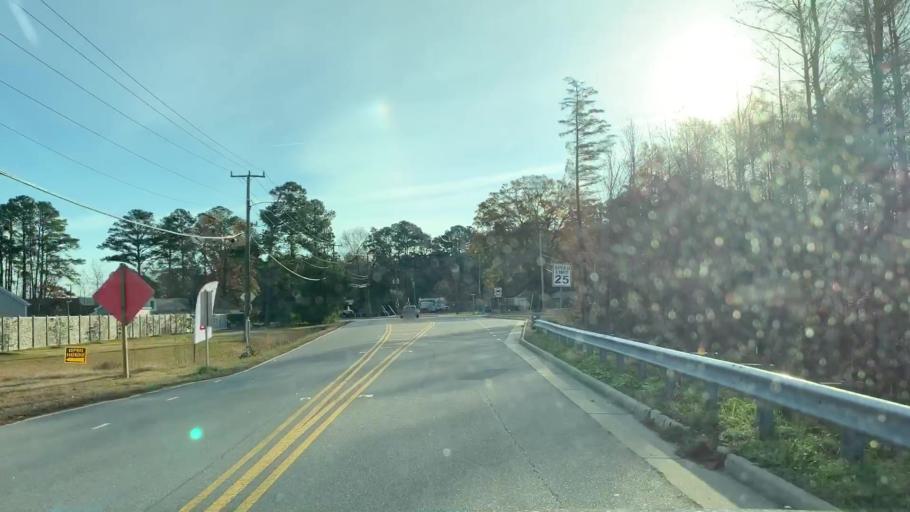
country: US
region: Virginia
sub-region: City of Chesapeake
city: Chesapeake
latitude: 36.7608
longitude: -76.1434
